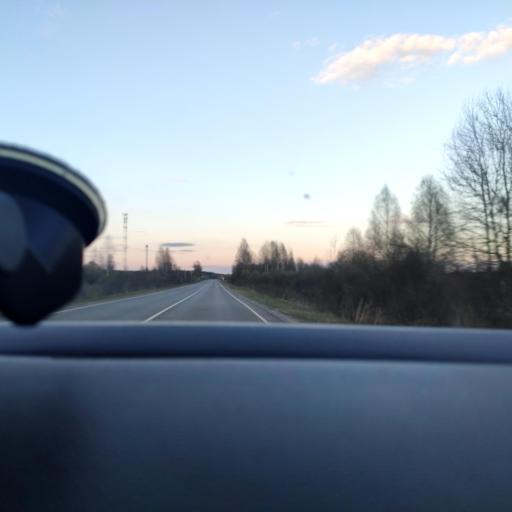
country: RU
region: Moskovskaya
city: Shaturtorf
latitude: 55.4319
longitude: 39.4018
